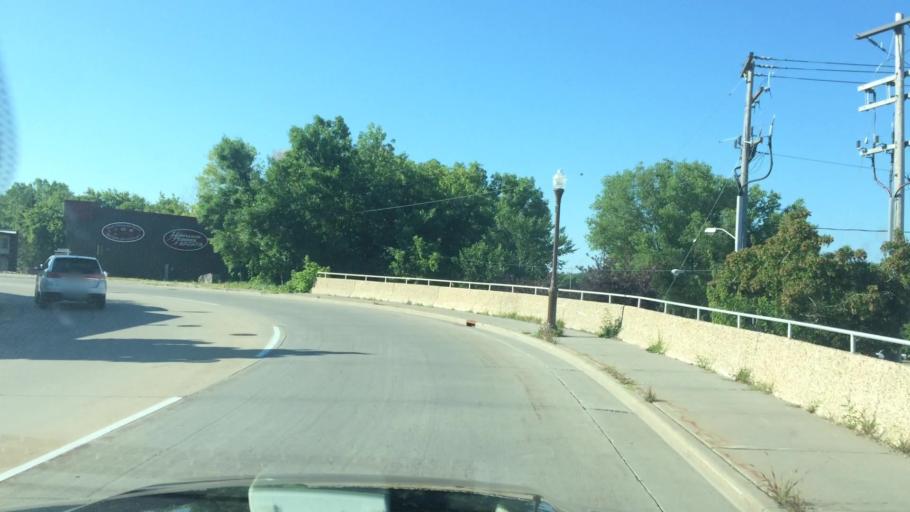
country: US
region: Wisconsin
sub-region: Marathon County
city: Wausau
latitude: 44.9578
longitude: -89.6307
